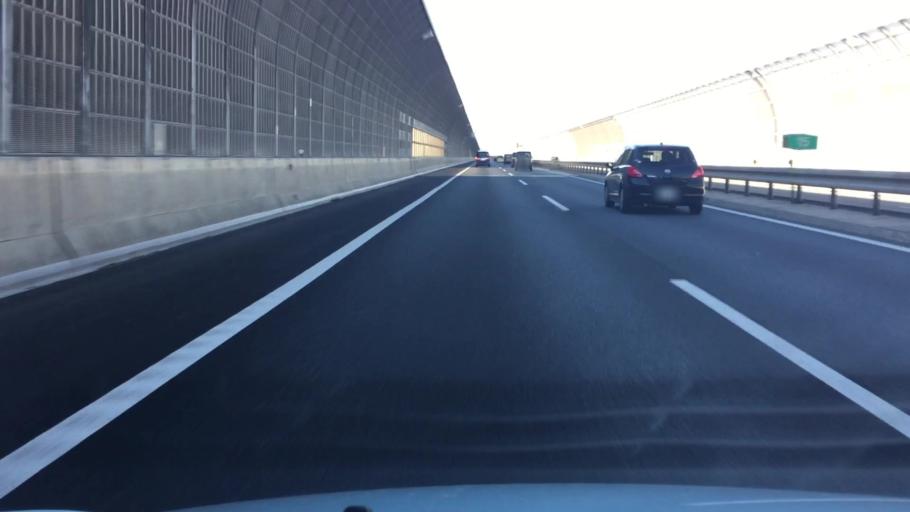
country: JP
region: Saitama
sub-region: Kawaguchi-shi
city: Hatogaya-honcho
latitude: 35.8478
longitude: 139.7076
